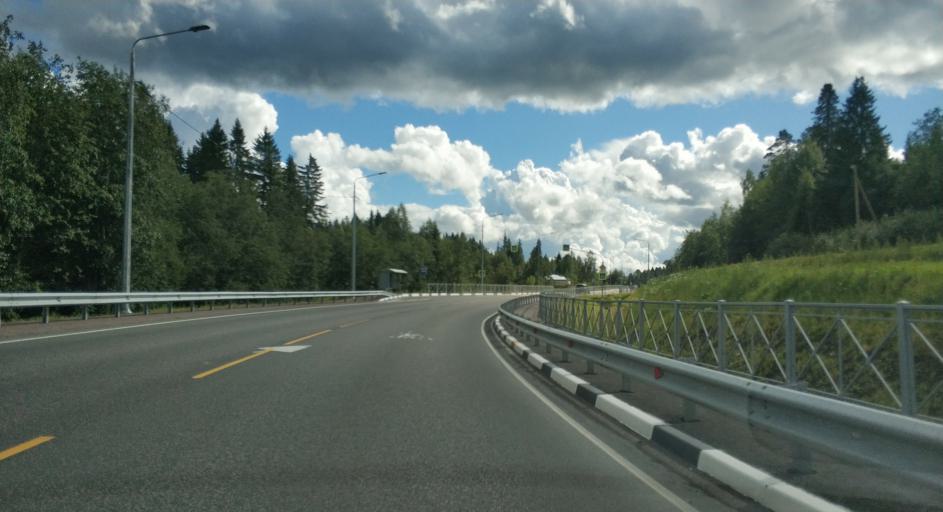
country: RU
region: Republic of Karelia
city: Ruskeala
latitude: 61.9309
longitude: 30.5964
